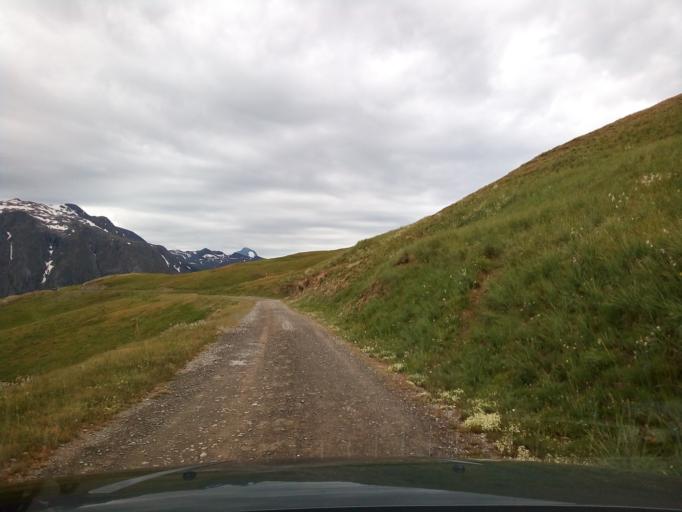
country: FR
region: Rhone-Alpes
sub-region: Departement de l'Isere
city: Mont-de-Lans
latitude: 45.0617
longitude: 6.2155
